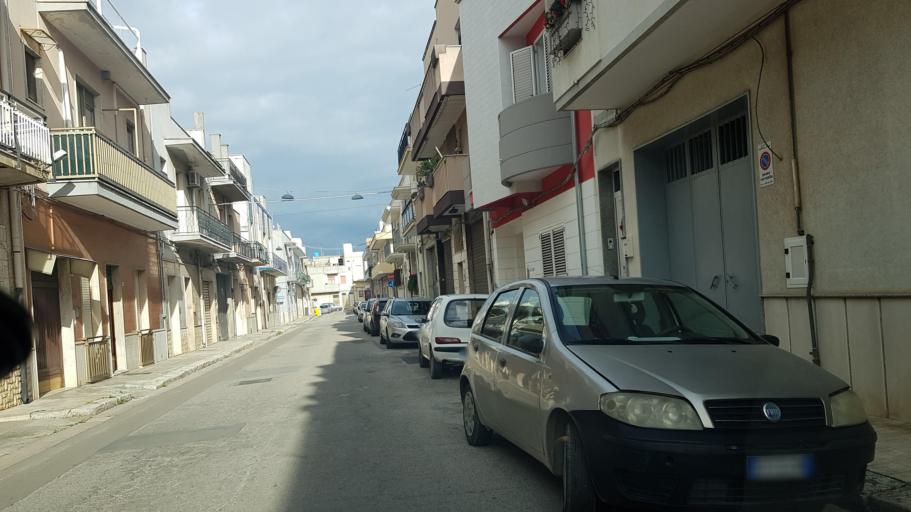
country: IT
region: Apulia
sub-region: Provincia di Brindisi
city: Francavilla Fontana
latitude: 40.5233
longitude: 17.5799
